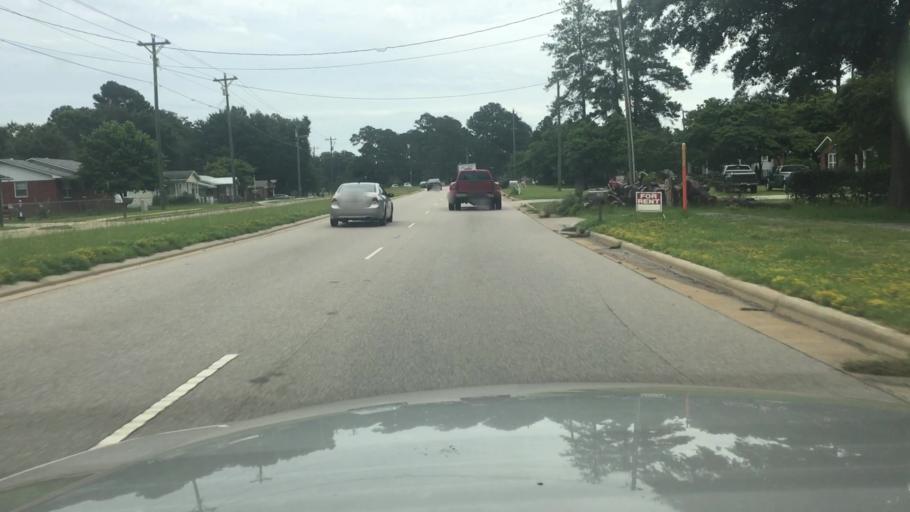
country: US
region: North Carolina
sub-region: Cumberland County
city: Hope Mills
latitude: 34.9929
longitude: -78.9639
